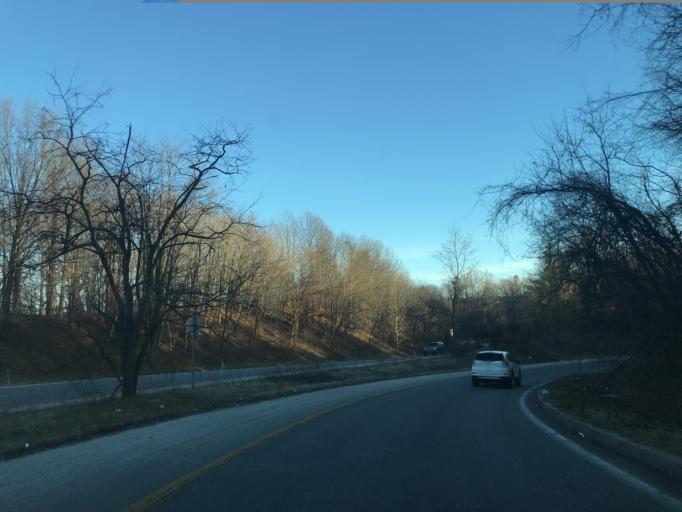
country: US
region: Maryland
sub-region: Anne Arundel County
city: Parole
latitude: 38.9730
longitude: -76.5409
